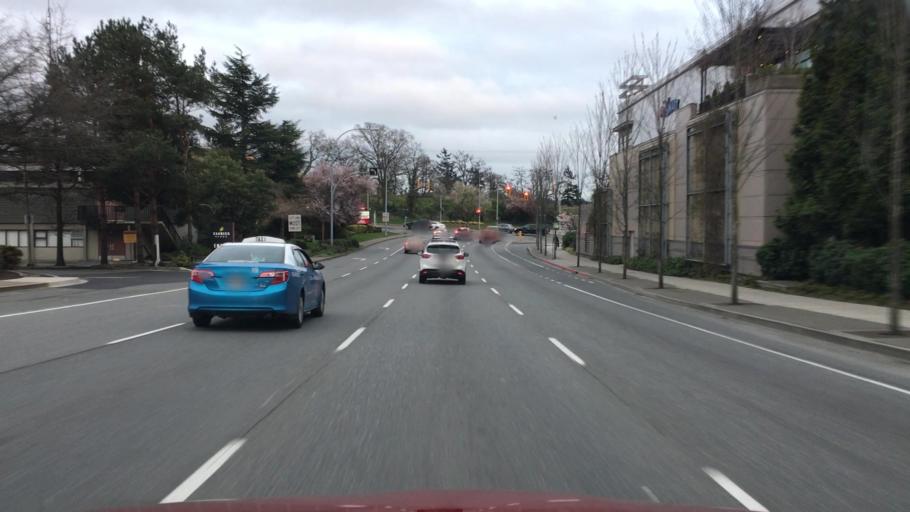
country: CA
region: British Columbia
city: Victoria
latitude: 48.4560
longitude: -123.3736
